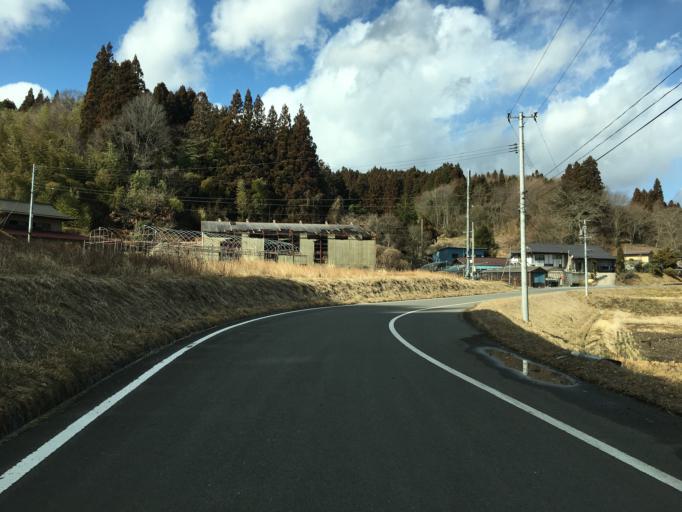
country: JP
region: Fukushima
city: Ishikawa
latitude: 37.2455
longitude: 140.5961
